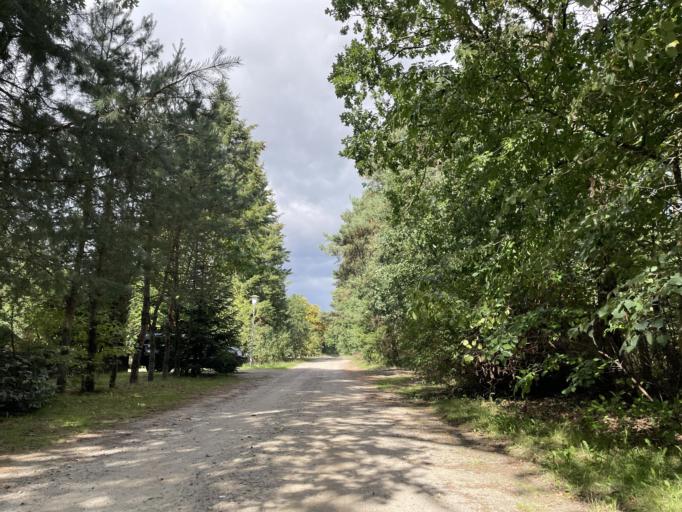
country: DE
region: Lower Saxony
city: Wendisch Evern
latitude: 53.2143
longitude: 10.4836
